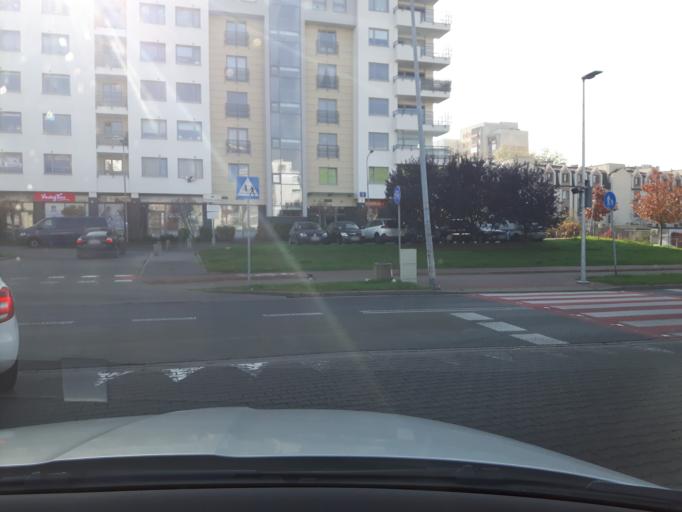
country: PL
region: Masovian Voivodeship
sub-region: Warszawa
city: Praga Poludnie
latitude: 52.2306
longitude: 21.1040
